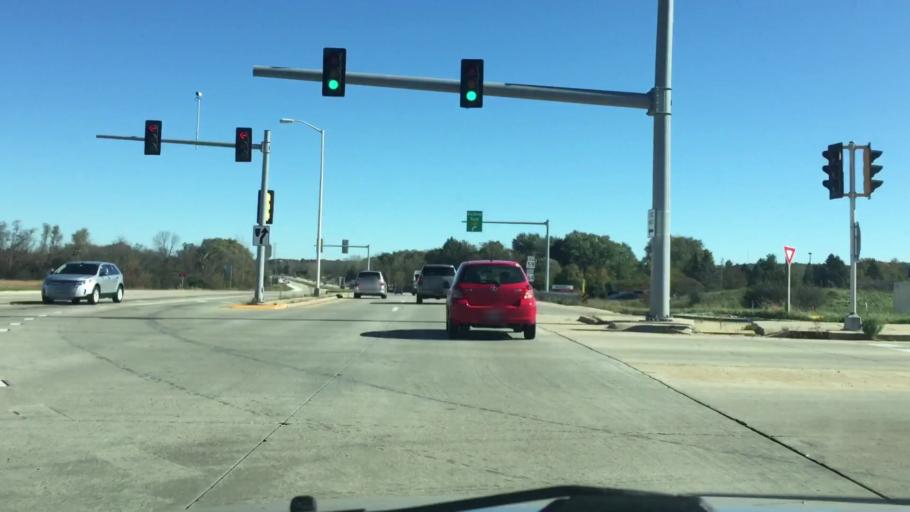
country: US
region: Wisconsin
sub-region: Waukesha County
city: Waukesha
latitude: 42.9773
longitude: -88.2275
